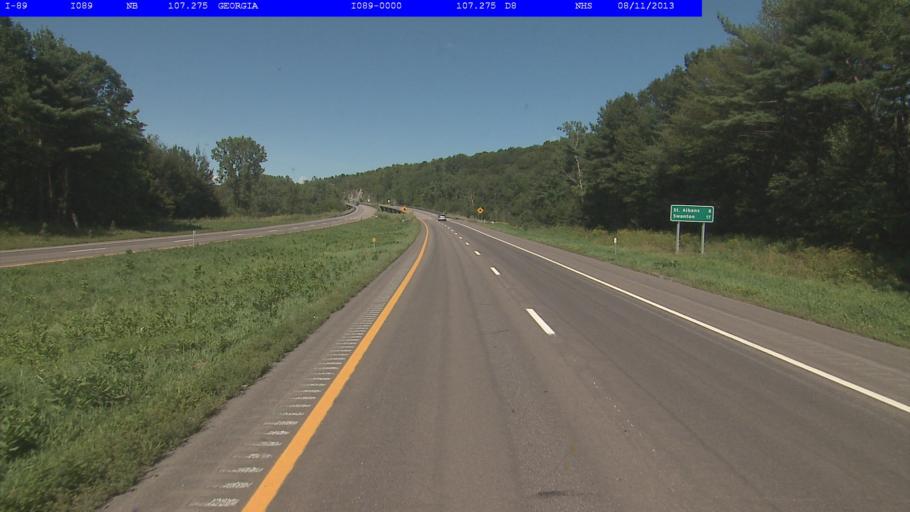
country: US
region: Vermont
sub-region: Chittenden County
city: Milton
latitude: 44.7038
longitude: -73.0936
